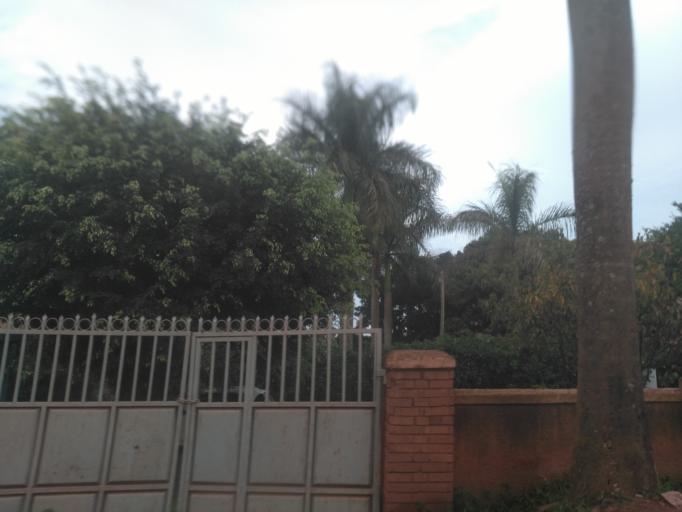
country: UG
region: Central Region
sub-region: Wakiso District
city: Kireka
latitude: 0.3760
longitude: 32.6161
